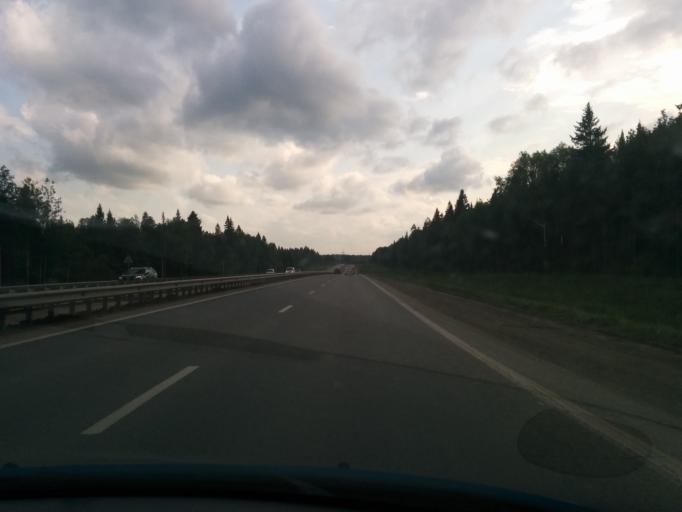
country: RU
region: Perm
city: Ferma
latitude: 58.0242
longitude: 56.4236
